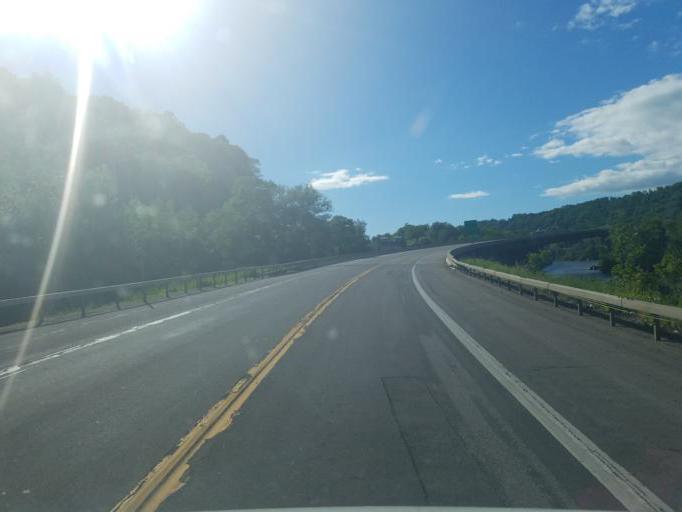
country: US
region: New York
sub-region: Herkimer County
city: Little Falls
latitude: 43.0365
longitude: -74.8426
